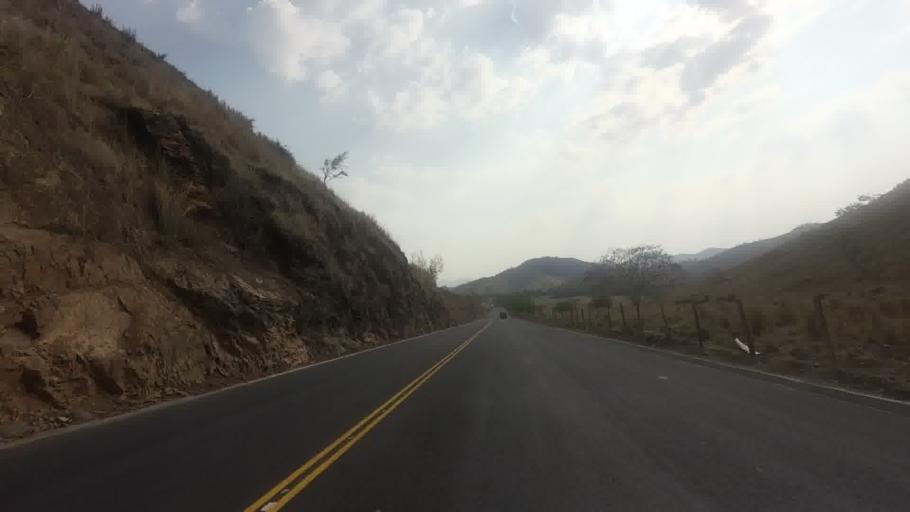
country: BR
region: Rio de Janeiro
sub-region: Itaperuna
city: Itaperuna
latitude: -21.2960
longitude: -41.8330
